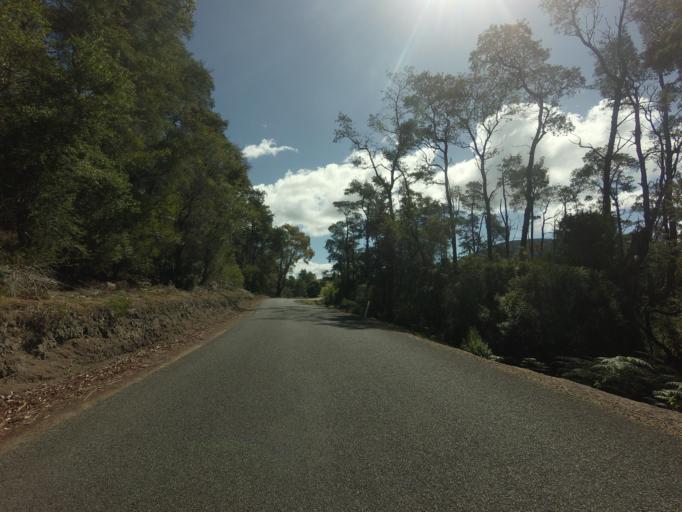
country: AU
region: Tasmania
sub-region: Break O'Day
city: St Helens
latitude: -41.6495
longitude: 148.2437
